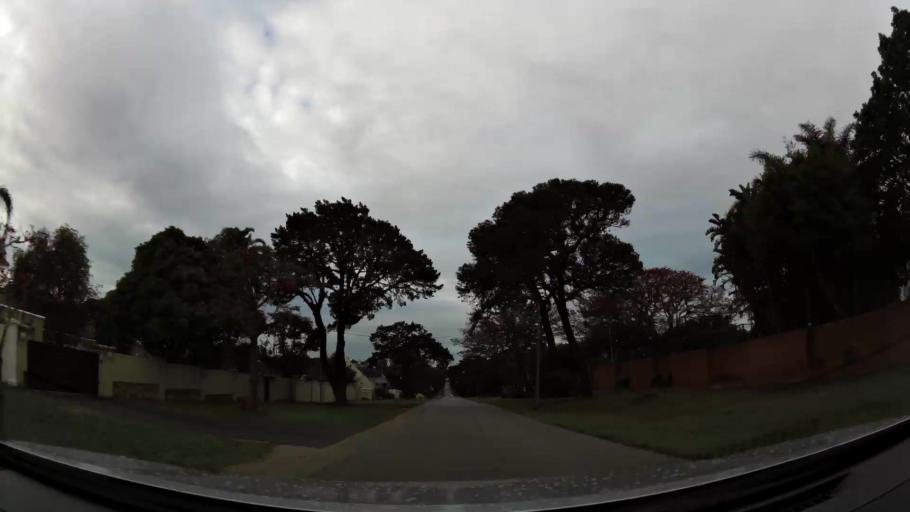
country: ZA
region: Eastern Cape
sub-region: Nelson Mandela Bay Metropolitan Municipality
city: Port Elizabeth
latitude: -33.9755
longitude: 25.5808
